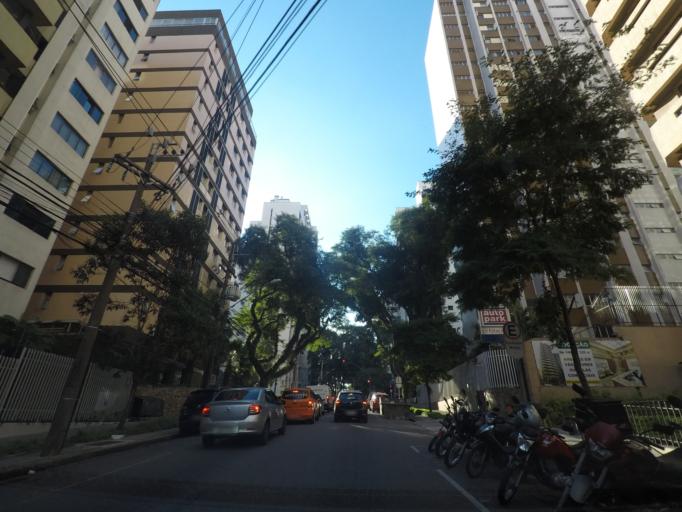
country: BR
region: Parana
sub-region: Curitiba
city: Curitiba
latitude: -25.4472
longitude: -49.2902
